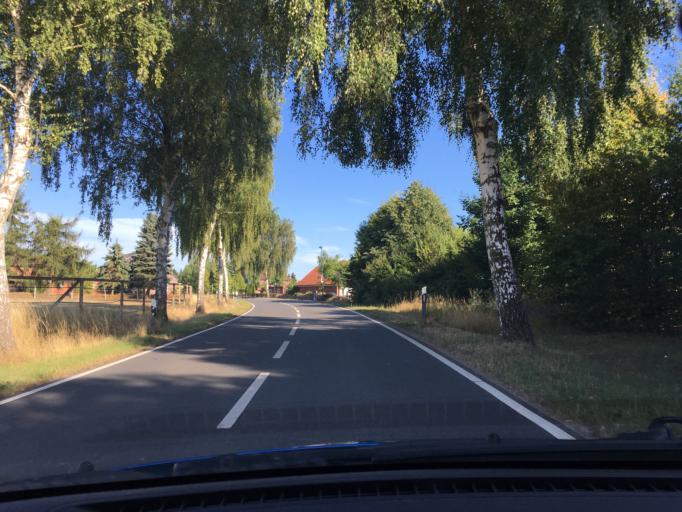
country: DE
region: Lower Saxony
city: Dahlenburg
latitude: 53.1921
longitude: 10.7216
